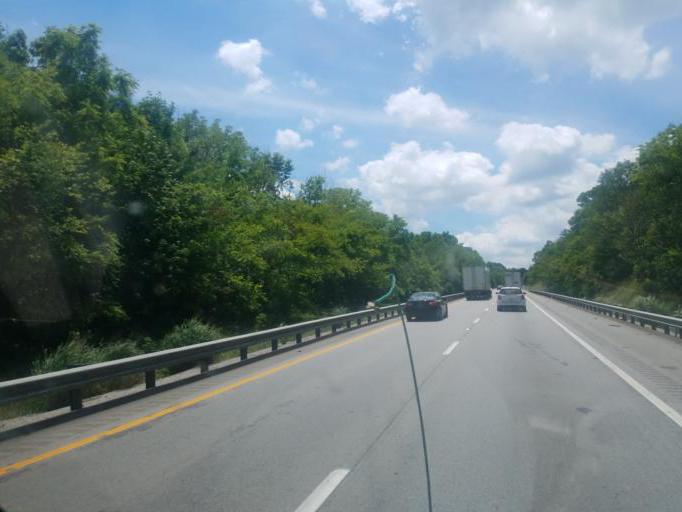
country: US
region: Kentucky
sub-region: Trimble County
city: Providence
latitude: 38.4783
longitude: -85.2718
